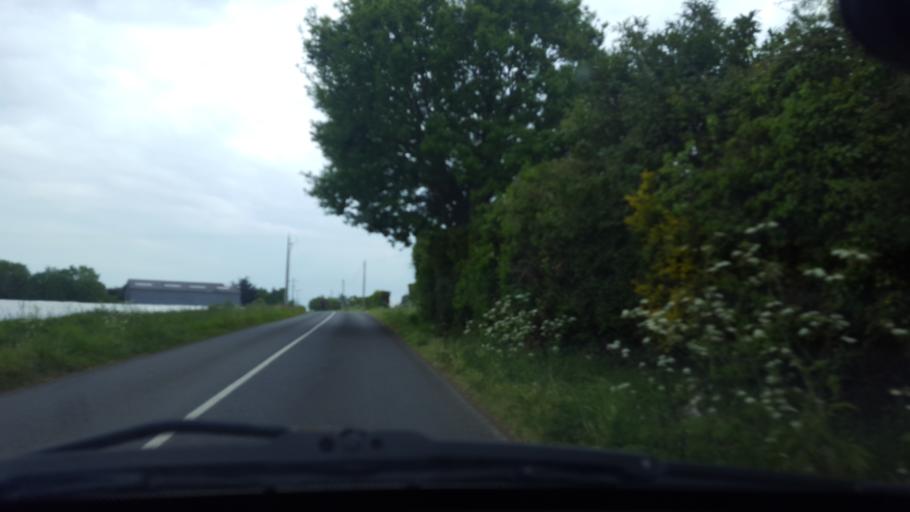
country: FR
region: Pays de la Loire
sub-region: Departement de la Loire-Atlantique
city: Saint-Philbert-de-Grand-Lieu
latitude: 47.0243
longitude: -1.6338
